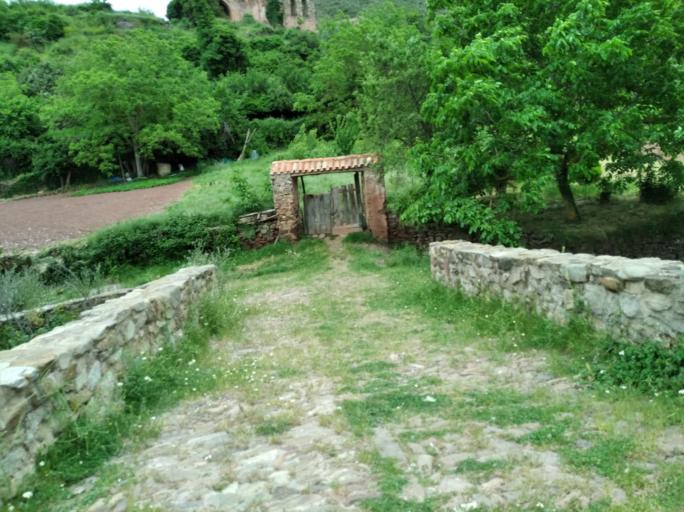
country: ES
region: La Rioja
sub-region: Provincia de La Rioja
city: Robres del Castillo
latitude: 42.2728
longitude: -2.2923
